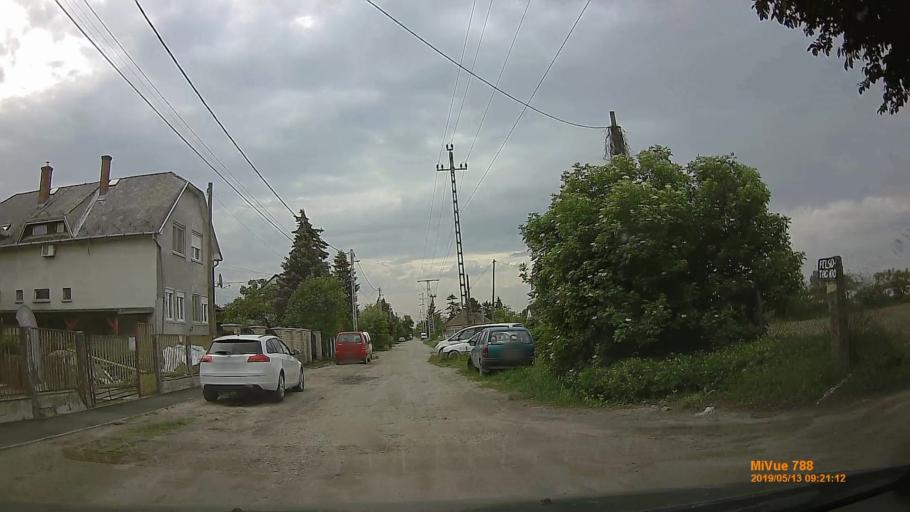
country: HU
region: Budapest
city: Budapest XXIII. keruelet
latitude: 47.4002
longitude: 19.0866
